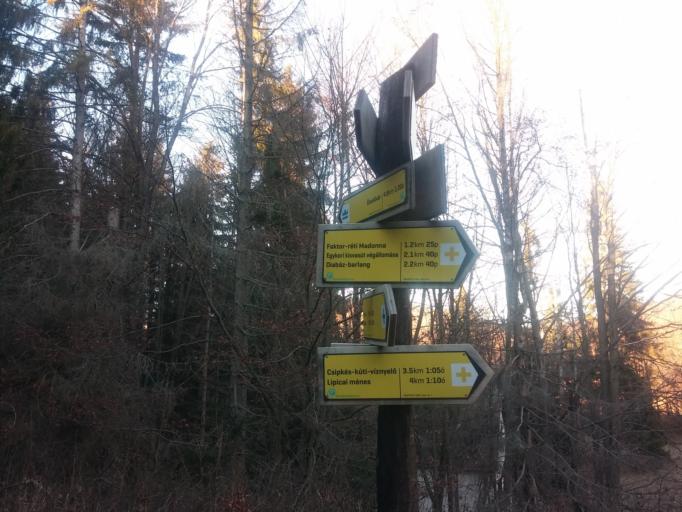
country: HU
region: Heves
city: Szilvasvarad
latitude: 48.0834
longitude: 20.4641
